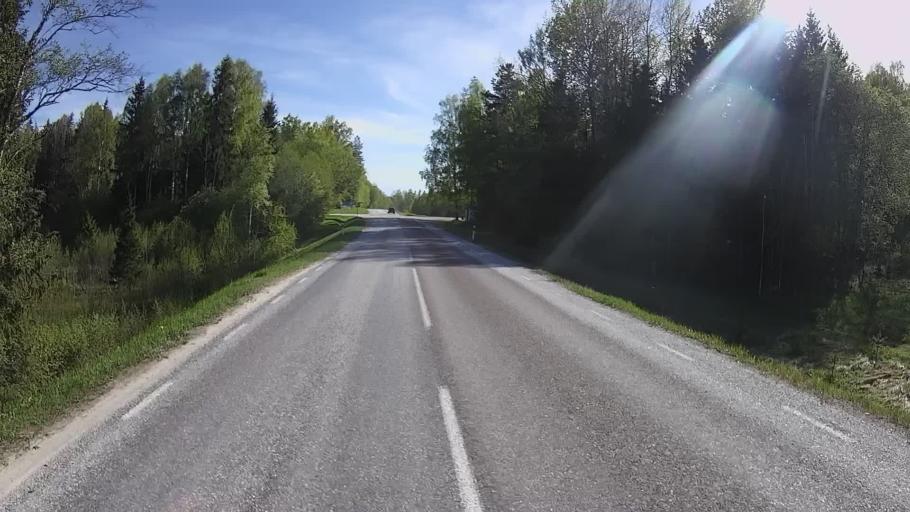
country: EE
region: Vorumaa
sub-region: Antsla vald
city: Vana-Antsla
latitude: 57.9976
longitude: 26.4955
